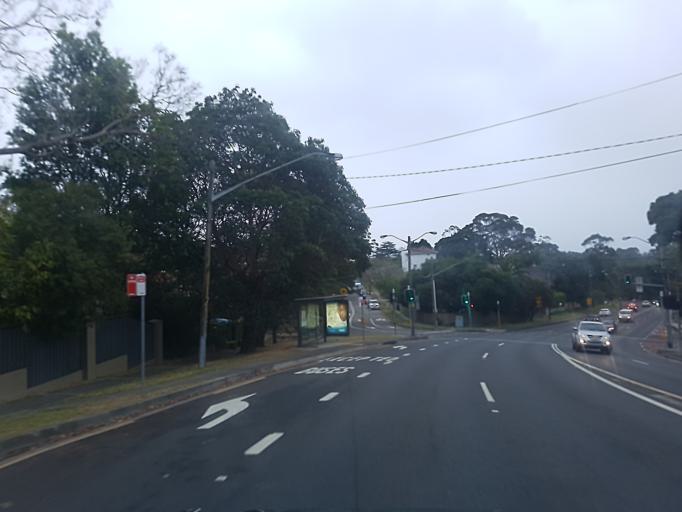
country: AU
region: New South Wales
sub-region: Willoughby
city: Castle Cove
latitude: -33.7919
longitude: 151.2070
